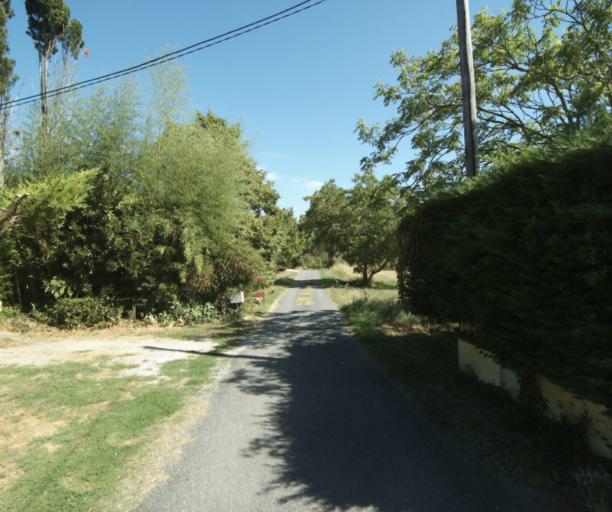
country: FR
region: Midi-Pyrenees
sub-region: Departement de la Haute-Garonne
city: Saint-Felix-Lauragais
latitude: 43.5163
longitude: 1.8957
